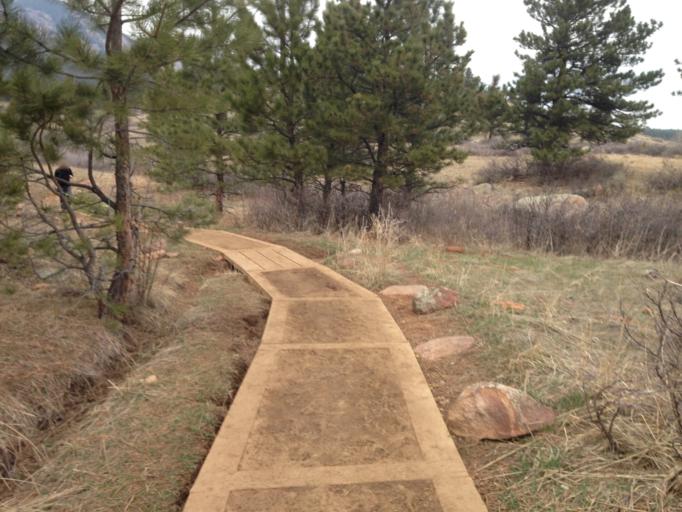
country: US
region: Colorado
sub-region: Boulder County
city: Boulder
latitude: 39.9481
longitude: -105.2669
